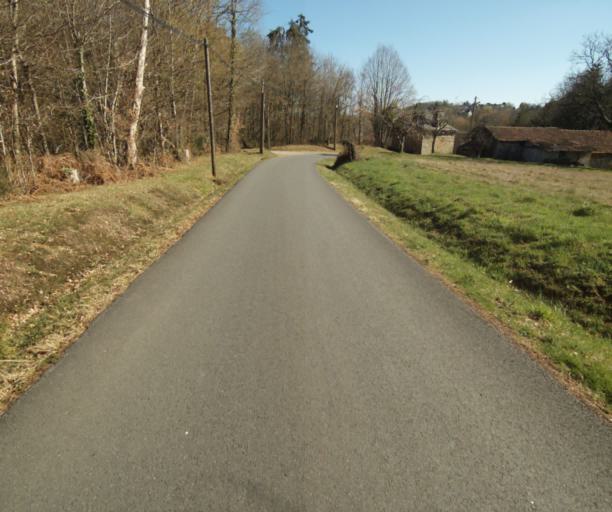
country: FR
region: Limousin
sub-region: Departement de la Correze
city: Tulle
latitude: 45.2747
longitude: 1.7277
